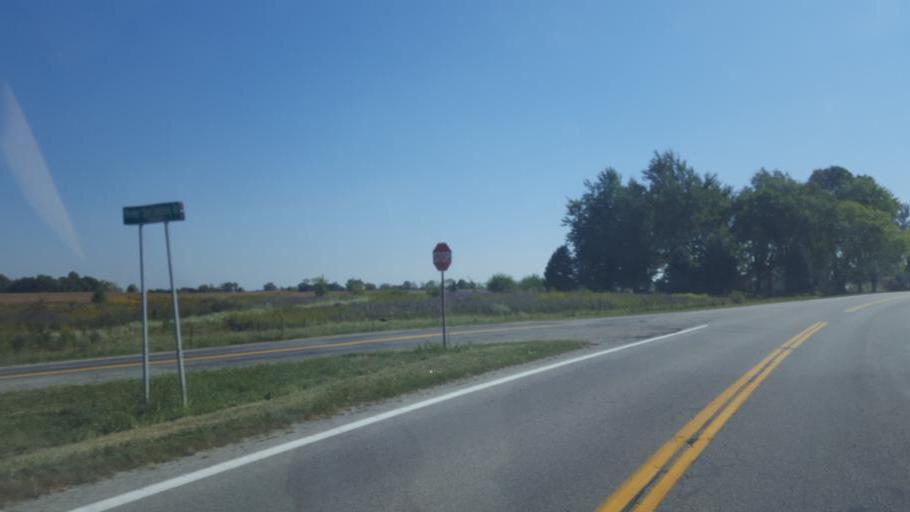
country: US
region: Ohio
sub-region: Marion County
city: Marion
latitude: 40.6433
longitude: -83.2931
